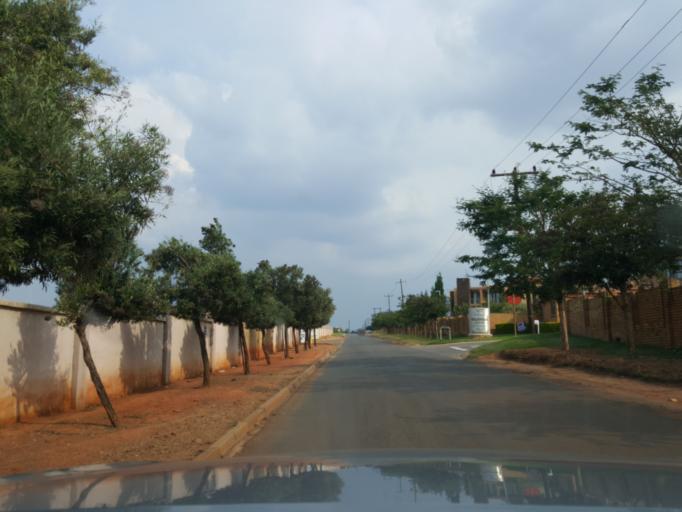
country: ZA
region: Gauteng
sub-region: City of Tshwane Metropolitan Municipality
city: Centurion
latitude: -25.8554
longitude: 28.3254
